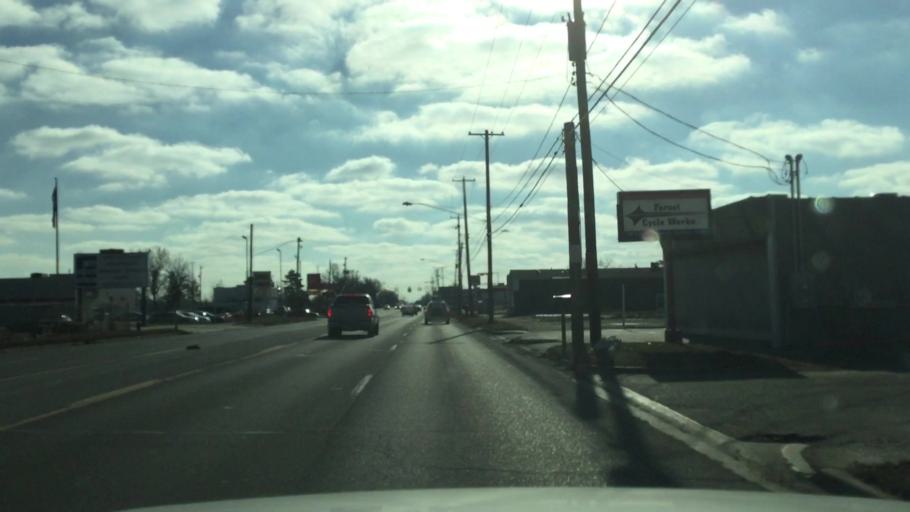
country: US
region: Michigan
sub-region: Genesee County
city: Flint
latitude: 43.0353
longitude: -83.6555
